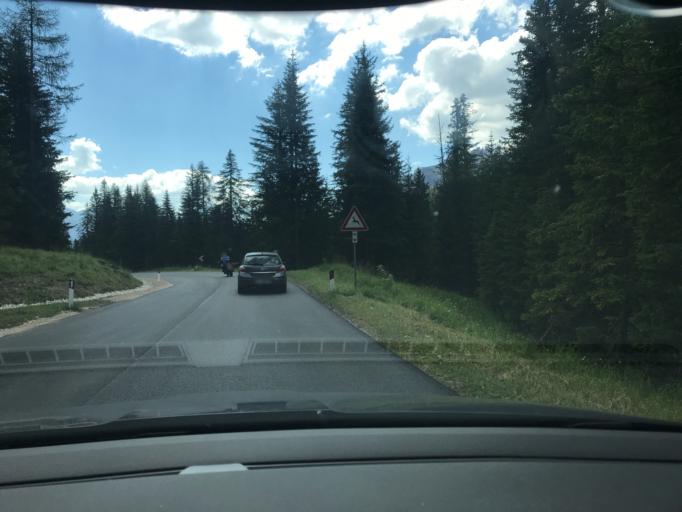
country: IT
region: Veneto
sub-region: Provincia di Belluno
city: Cortina d'Ampezzo
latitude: 46.5216
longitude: 12.0691
